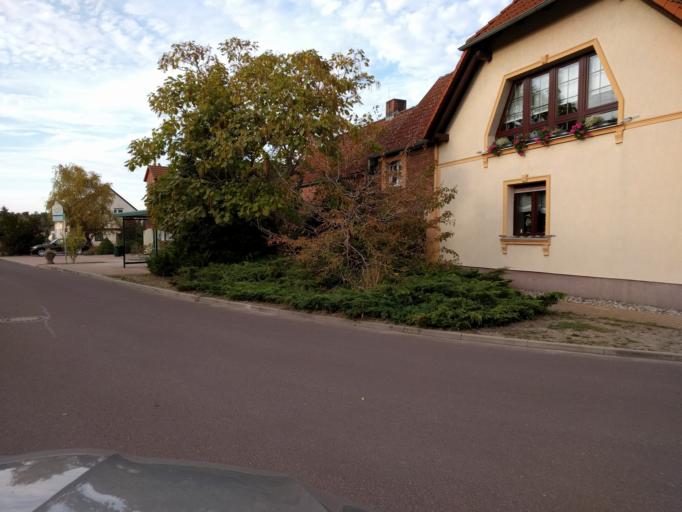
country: DE
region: Brandenburg
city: Ziesar
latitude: 52.2132
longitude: 12.2843
